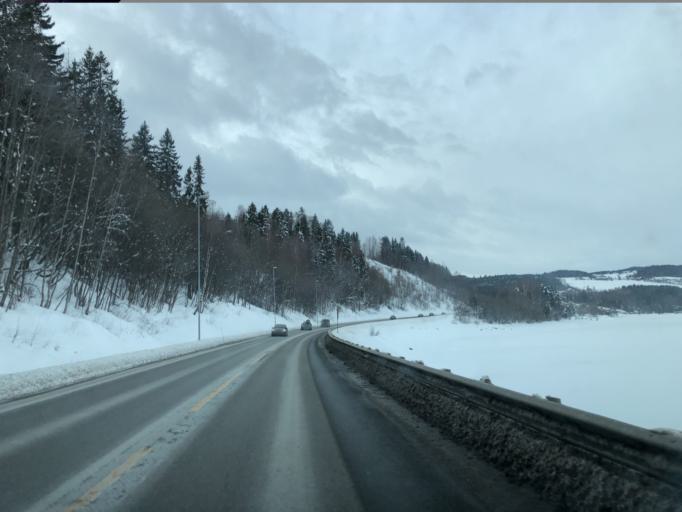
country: NO
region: Oppland
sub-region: Gjovik
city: Gjovik
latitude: 60.8096
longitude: 10.6831
